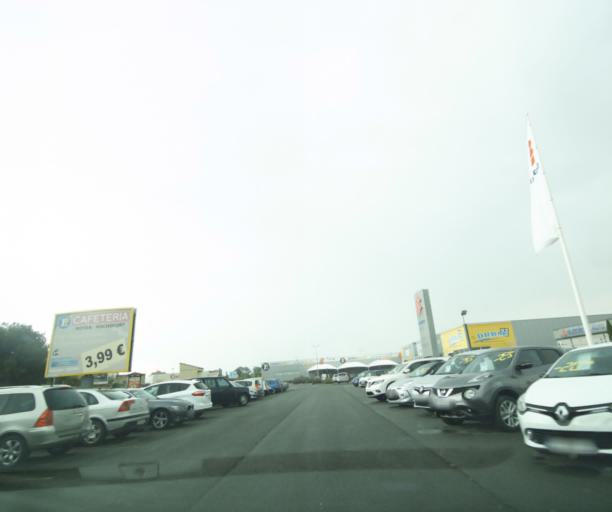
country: FR
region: Poitou-Charentes
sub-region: Departement de la Charente-Maritime
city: Tonnay-Charente
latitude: 45.9513
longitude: -0.9304
